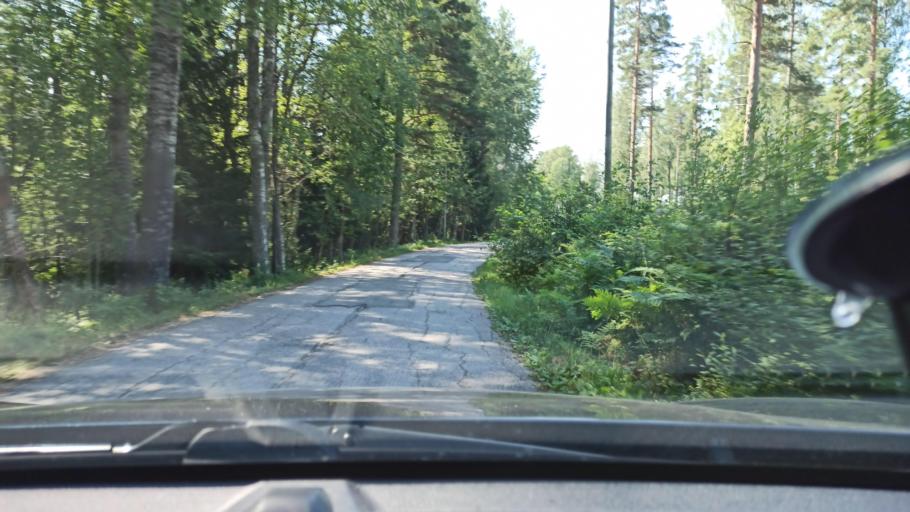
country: FI
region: Uusimaa
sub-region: Helsinki
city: Espoo
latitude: 60.1524
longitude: 24.5674
